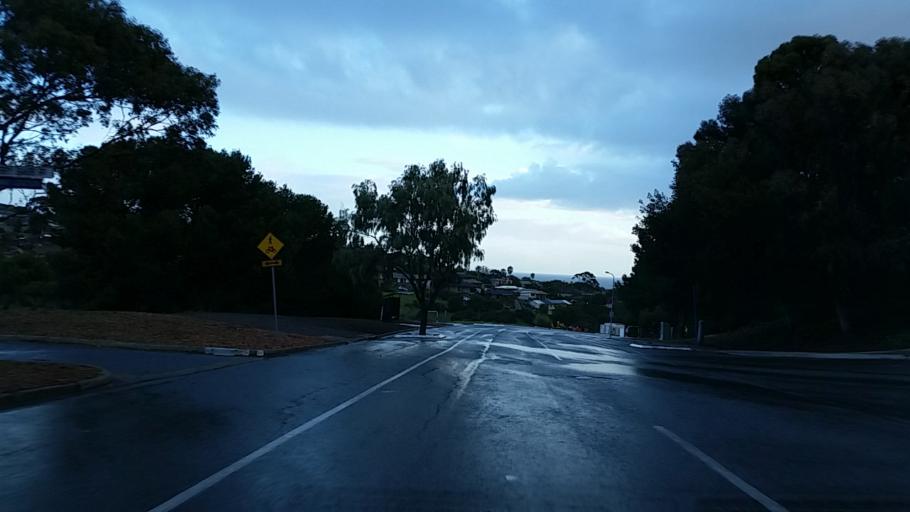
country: AU
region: South Australia
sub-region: Marion
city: Marino
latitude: -35.0700
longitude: 138.5105
